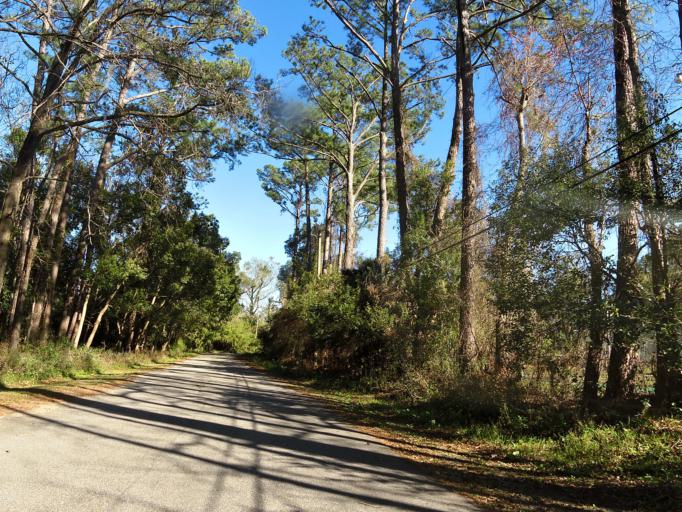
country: US
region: Florida
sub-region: Duval County
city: Jacksonville
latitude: 30.2819
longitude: -81.6494
